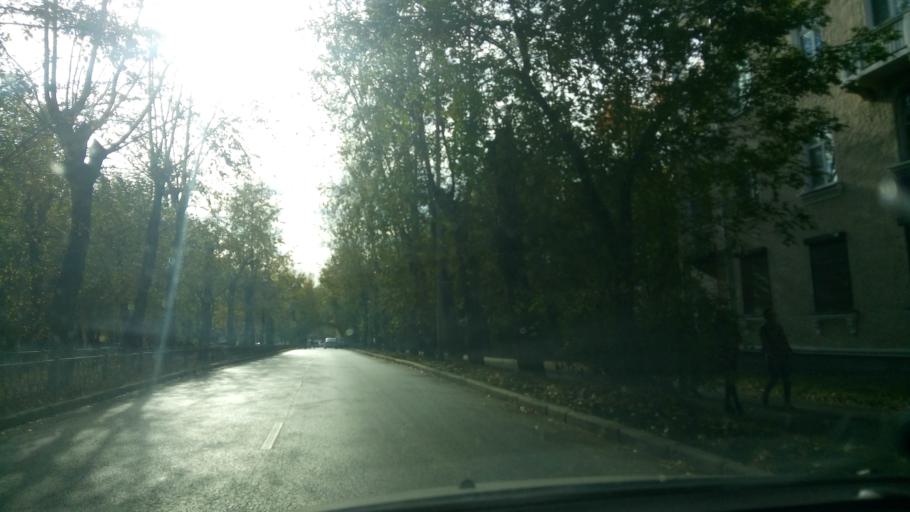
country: RU
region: Sverdlovsk
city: Yekaterinburg
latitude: 56.8885
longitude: 60.6179
